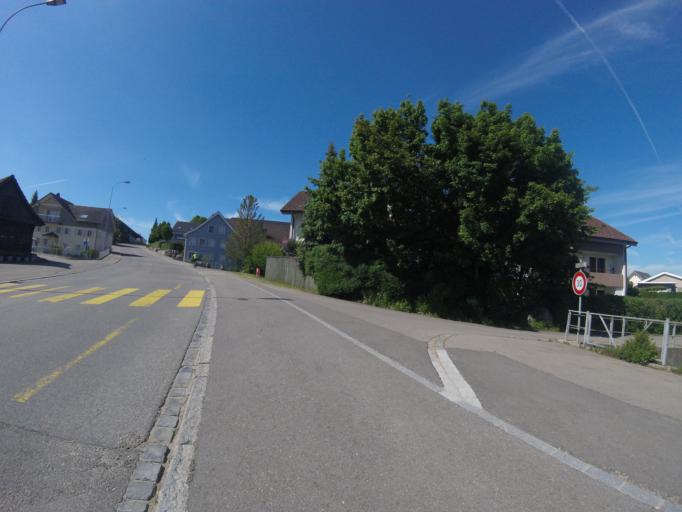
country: CH
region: Saint Gallen
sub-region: Wahlkreis Wil
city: Jonschwil
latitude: 47.4185
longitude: 9.0636
